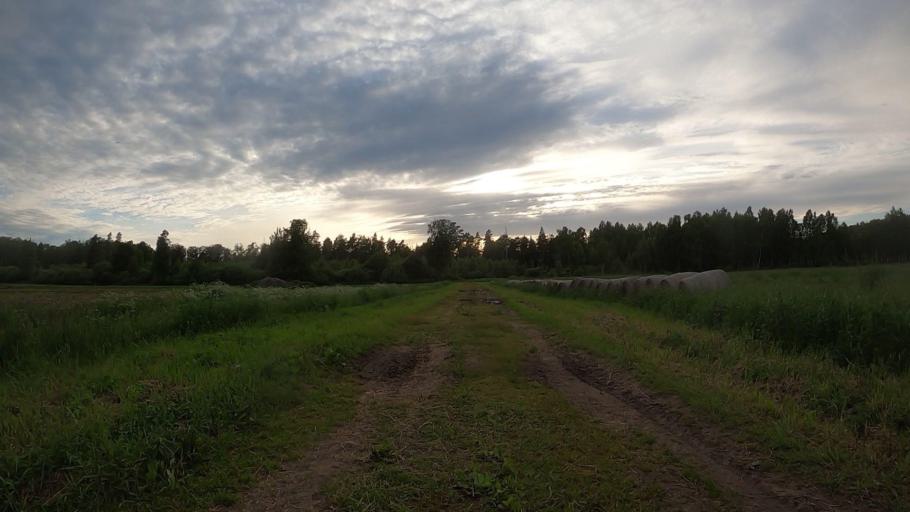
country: LV
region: Olaine
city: Olaine
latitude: 56.8260
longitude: 23.9427
